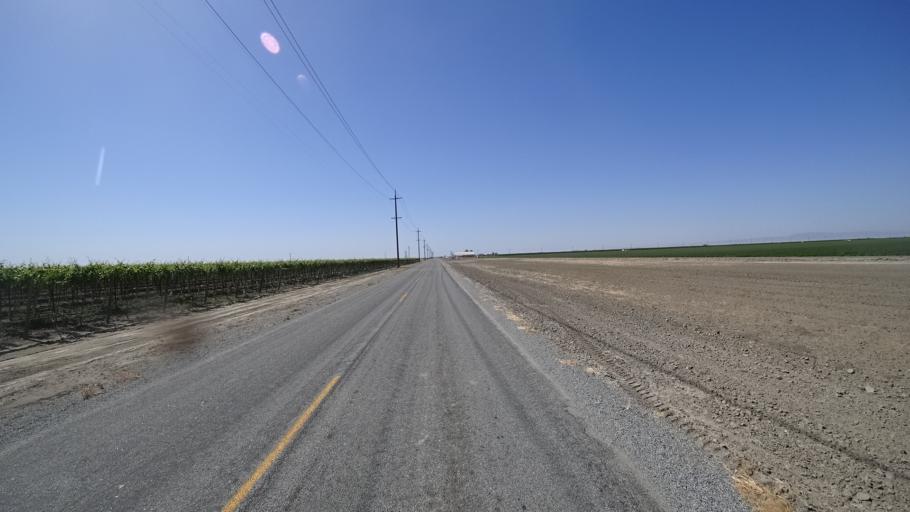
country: US
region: California
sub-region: Kings County
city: Stratford
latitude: 36.2359
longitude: -119.8343
